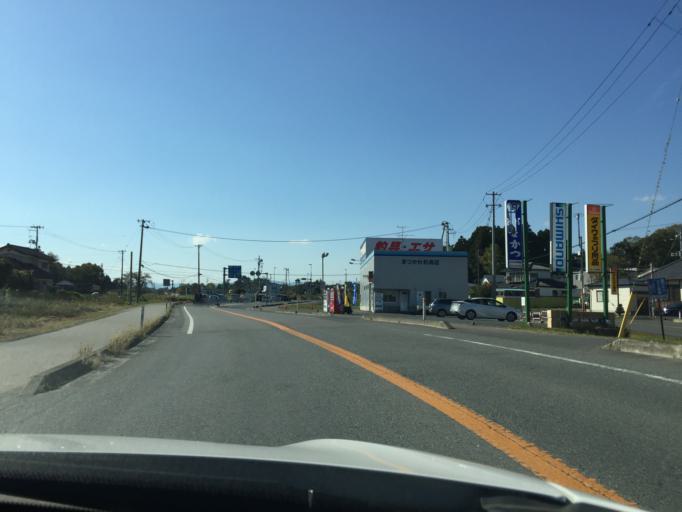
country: JP
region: Miyagi
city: Marumori
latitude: 37.8195
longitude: 140.9442
